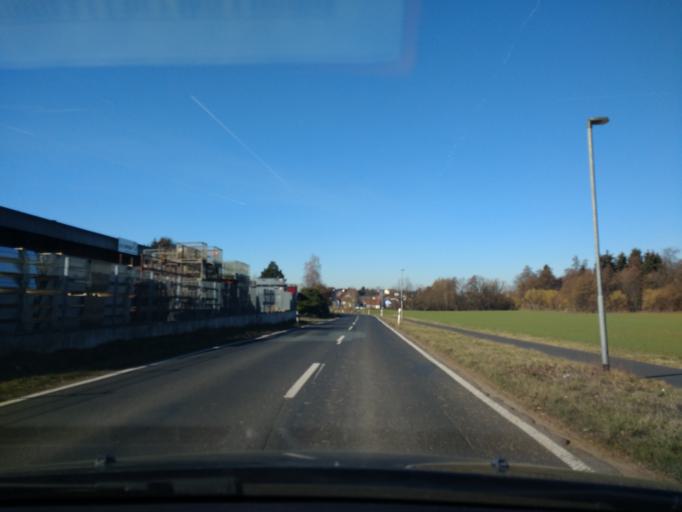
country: DE
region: Bavaria
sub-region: Regierungsbezirk Unterfranken
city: Geiselbach
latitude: 50.1377
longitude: 9.1545
